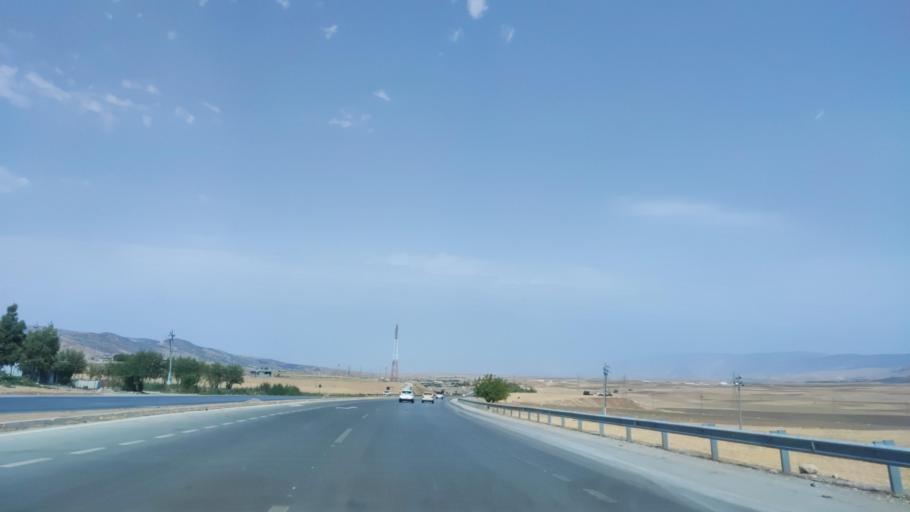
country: IQ
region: Arbil
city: Shaqlawah
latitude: 36.4930
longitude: 44.3702
